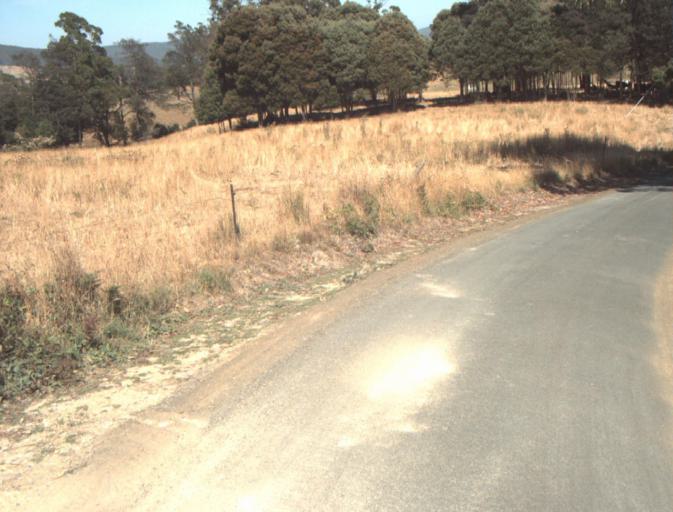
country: AU
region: Tasmania
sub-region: Launceston
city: Mayfield
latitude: -41.2316
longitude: 147.2432
